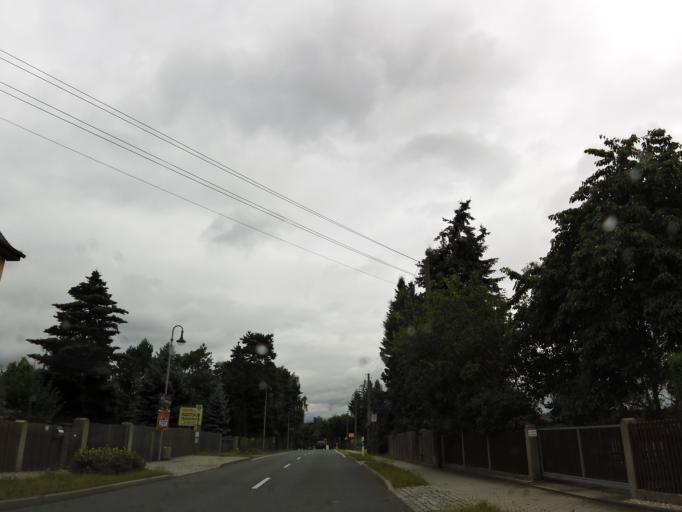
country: DE
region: Thuringia
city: Bad Klosterlausnitz
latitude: 50.9219
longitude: 11.8701
